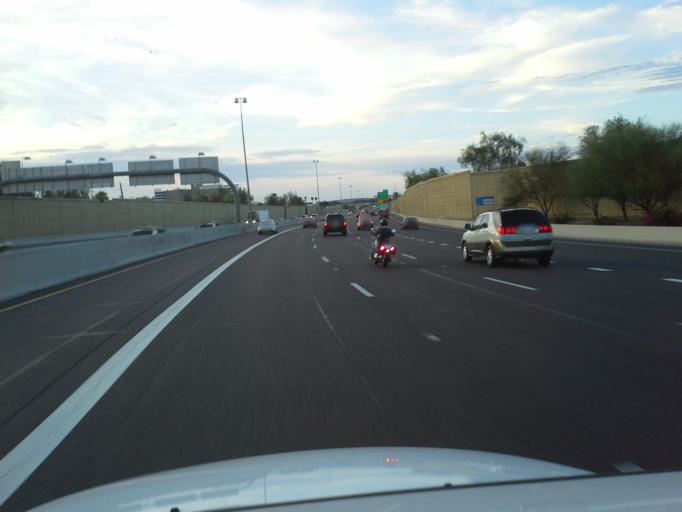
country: US
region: Arizona
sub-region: Maricopa County
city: Phoenix
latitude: 33.4688
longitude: -112.0384
